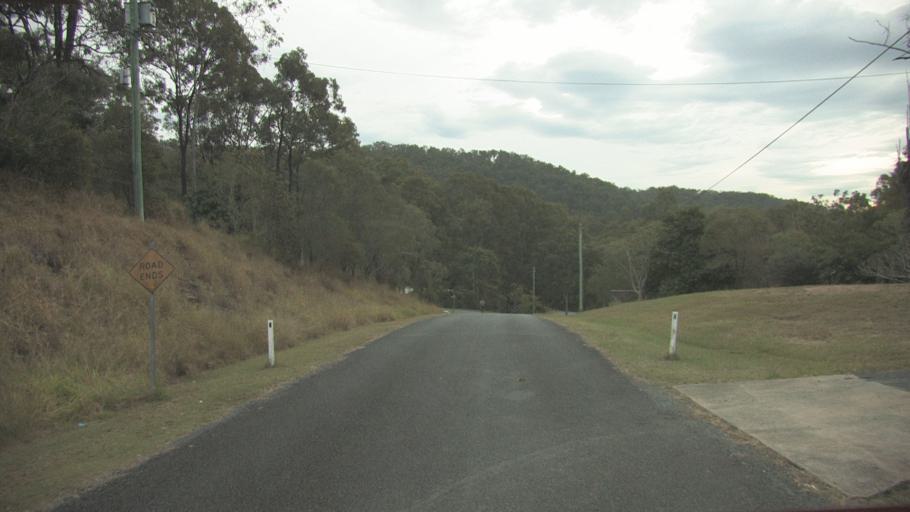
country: AU
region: Queensland
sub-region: Logan
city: Chambers Flat
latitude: -27.8251
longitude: 153.0927
